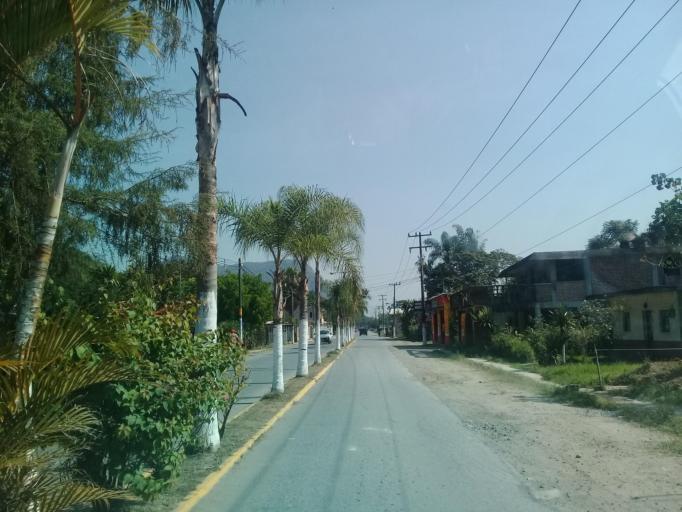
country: MX
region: Veracruz
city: Rafael Delgado
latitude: 18.7863
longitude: -97.0113
